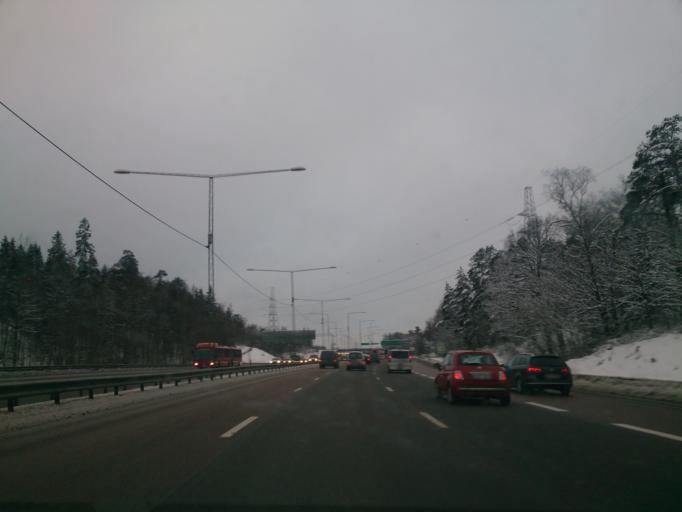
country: SE
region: Stockholm
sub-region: Huddinge Kommun
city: Segeltorp
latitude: 59.2680
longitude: 17.9071
